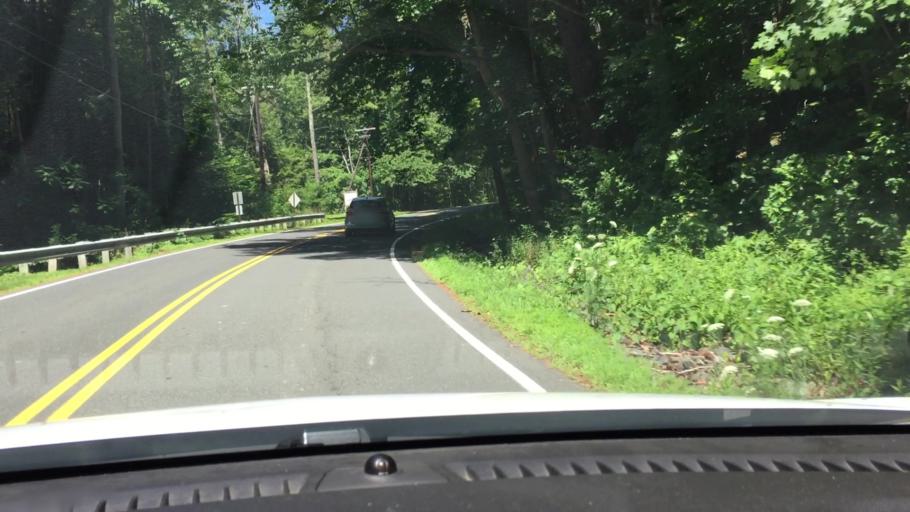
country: US
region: Massachusetts
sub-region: Berkshire County
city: Lenox
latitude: 42.3504
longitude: -73.2458
